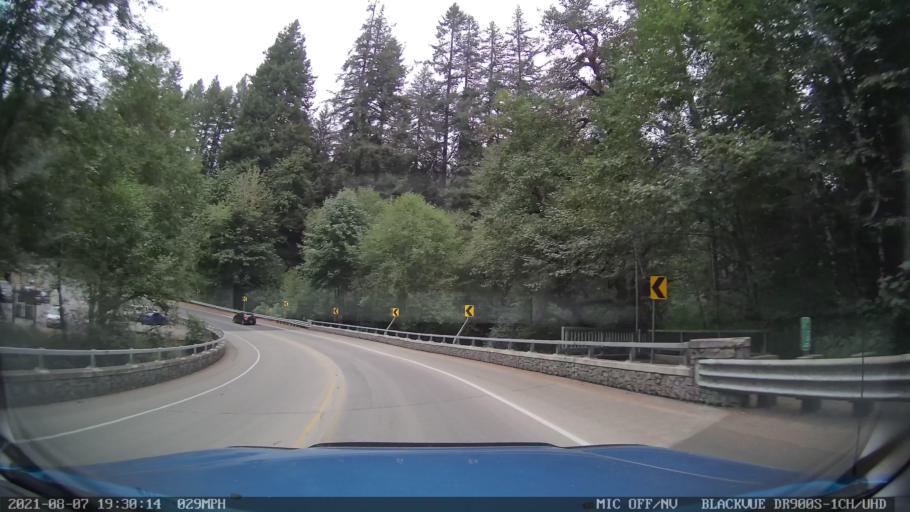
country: US
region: Oregon
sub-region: Linn County
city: Lyons
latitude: 44.8840
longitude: -122.6202
